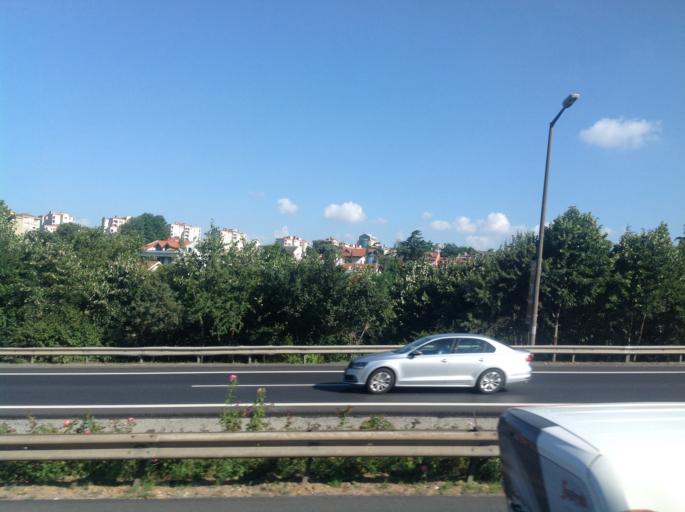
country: TR
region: Istanbul
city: Sisli
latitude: 41.0875
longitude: 29.0162
